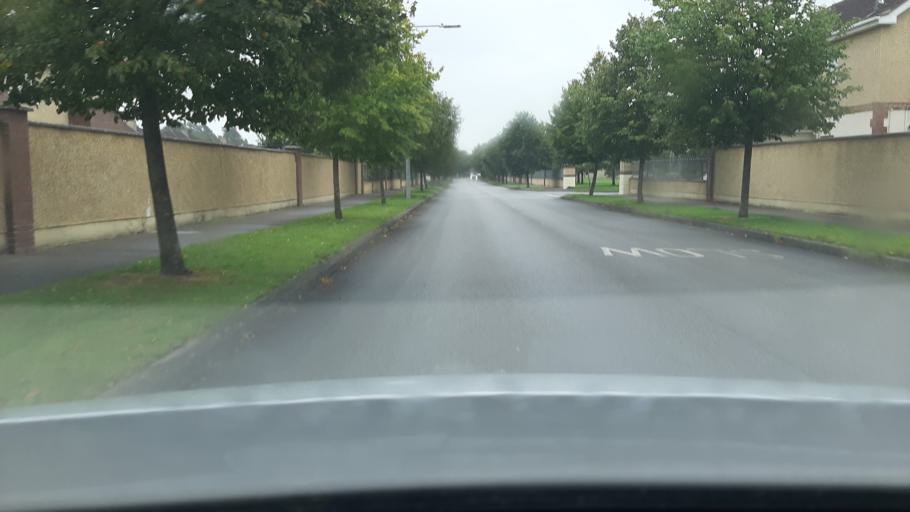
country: IE
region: Leinster
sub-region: Kildare
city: Kildare
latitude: 53.1567
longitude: -6.8954
